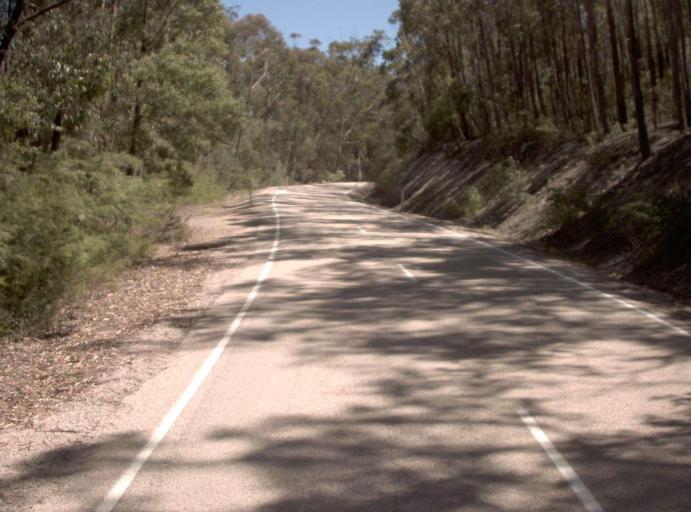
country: AU
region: Victoria
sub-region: East Gippsland
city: Lakes Entrance
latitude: -37.3173
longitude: 148.2448
